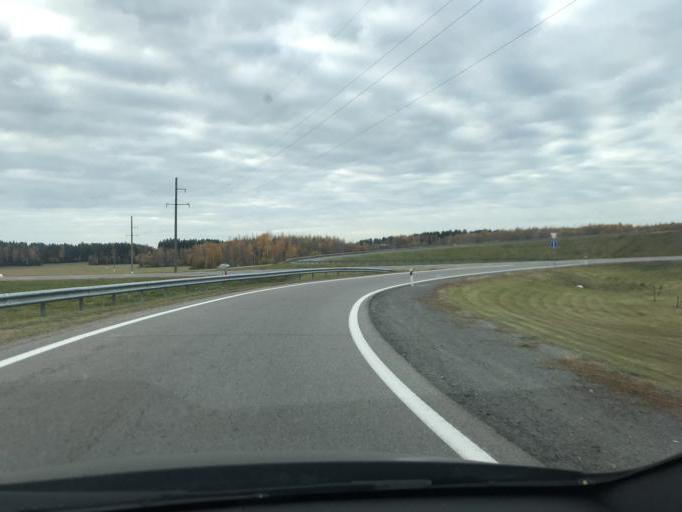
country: BY
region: Minsk
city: Astrashytski Haradok
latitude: 54.0553
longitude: 27.7072
